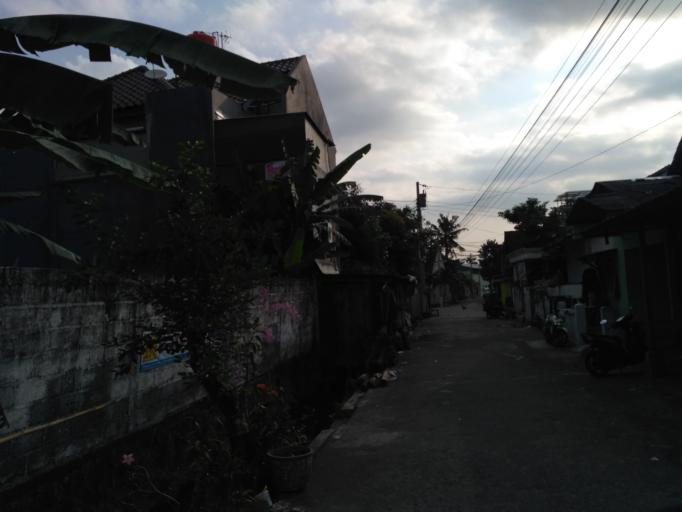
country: ID
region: Daerah Istimewa Yogyakarta
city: Melati
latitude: -7.7553
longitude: 110.3756
